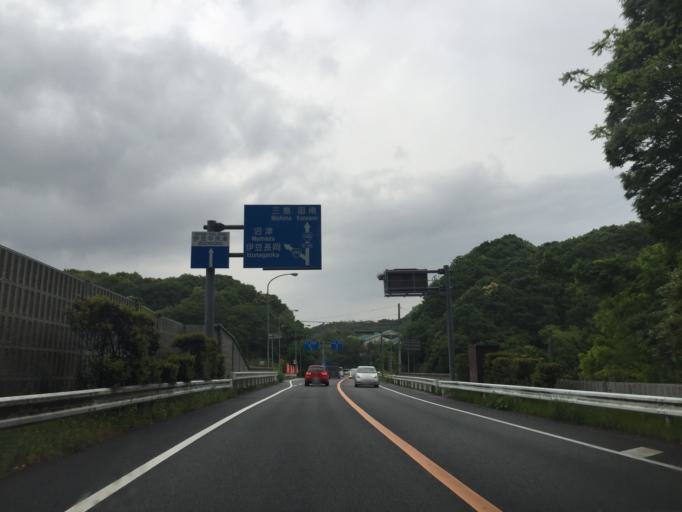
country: JP
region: Shizuoka
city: Mishima
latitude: 35.0391
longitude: 138.9207
